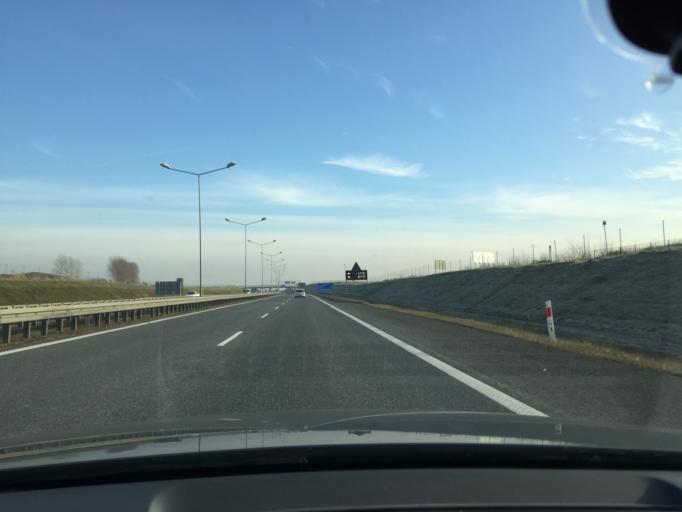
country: PL
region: Silesian Voivodeship
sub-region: Powiat gliwicki
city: Knurow
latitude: 50.2595
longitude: 18.6562
